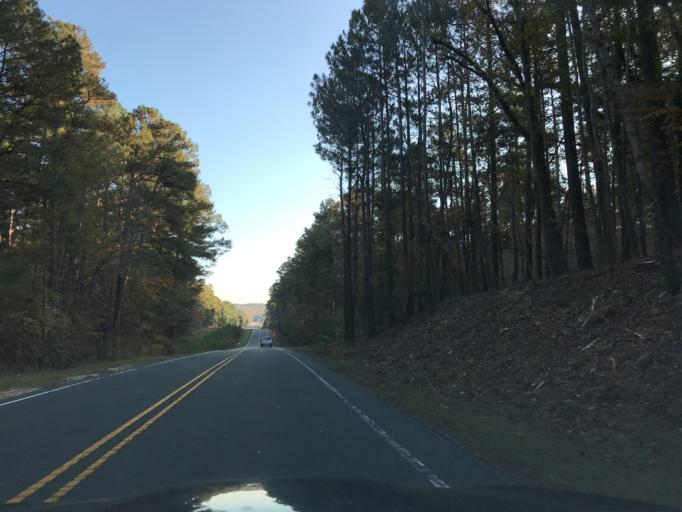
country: US
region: North Carolina
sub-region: Granville County
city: Creedmoor
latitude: 36.0267
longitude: -78.6973
